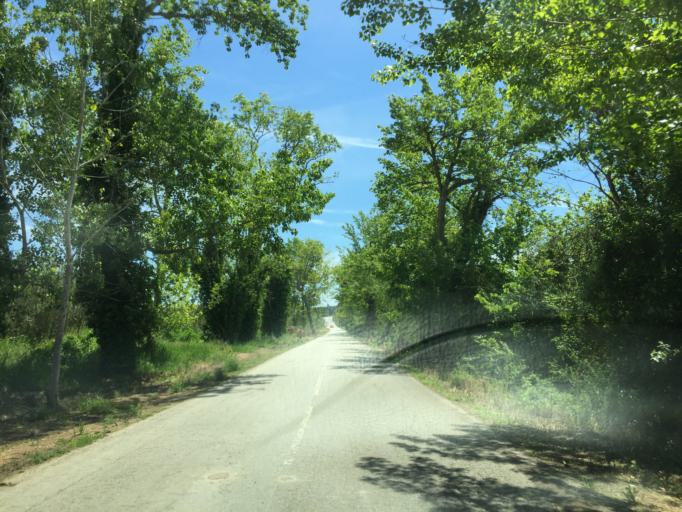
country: PT
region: Leiria
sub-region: Pombal
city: Lourical
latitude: 40.0703
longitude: -8.7329
